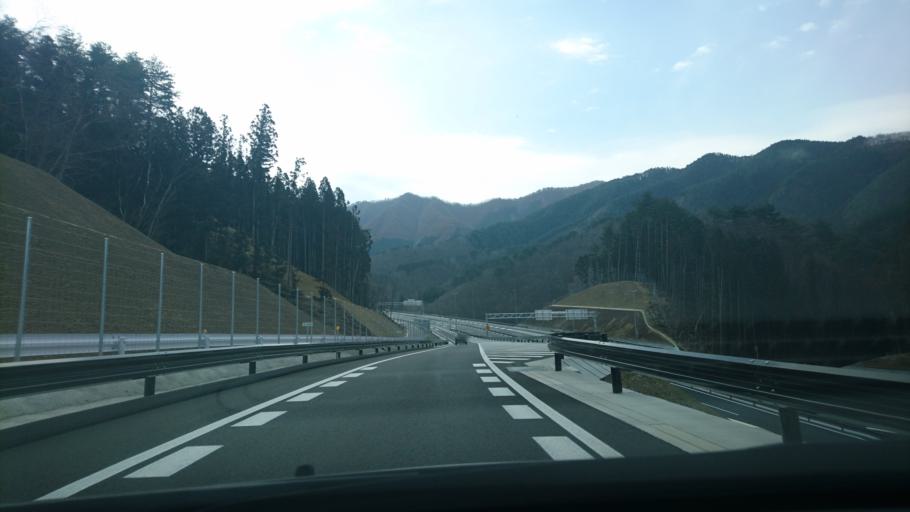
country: JP
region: Iwate
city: Kamaishi
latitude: 39.2542
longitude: 141.8373
